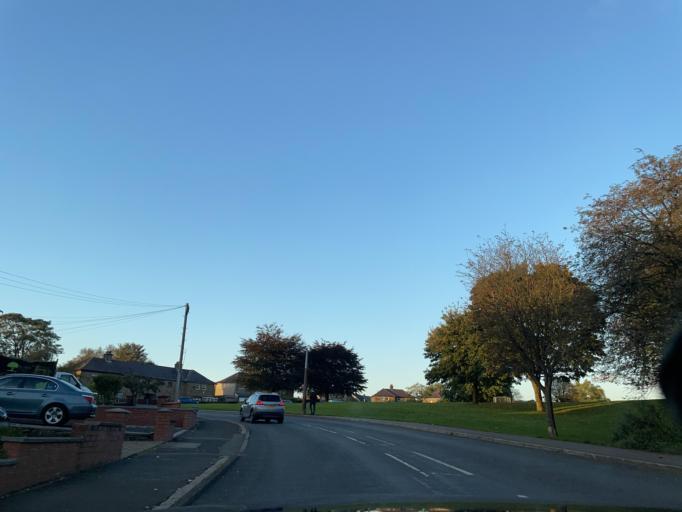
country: GB
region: England
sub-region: Borough of Tameside
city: Longdendale
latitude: 53.4542
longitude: -1.9770
